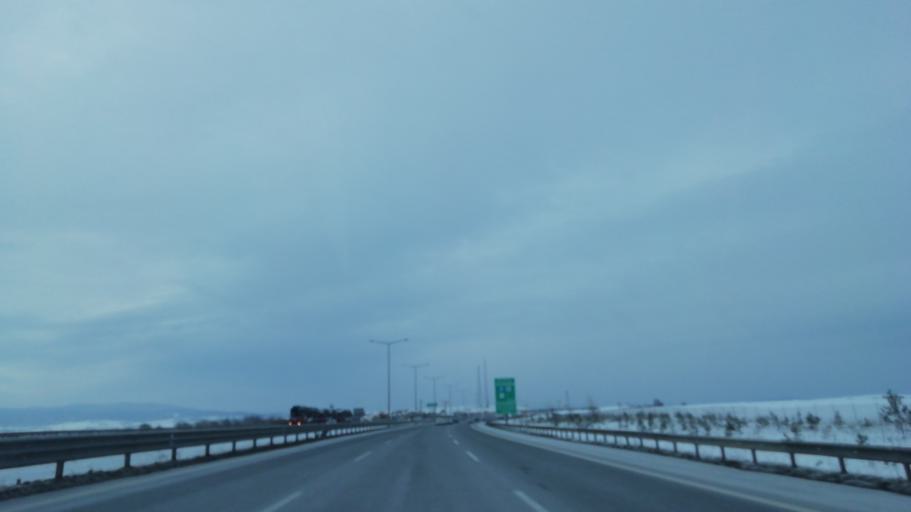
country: TR
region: Bolu
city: Dortdivan
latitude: 40.7475
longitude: 32.0917
